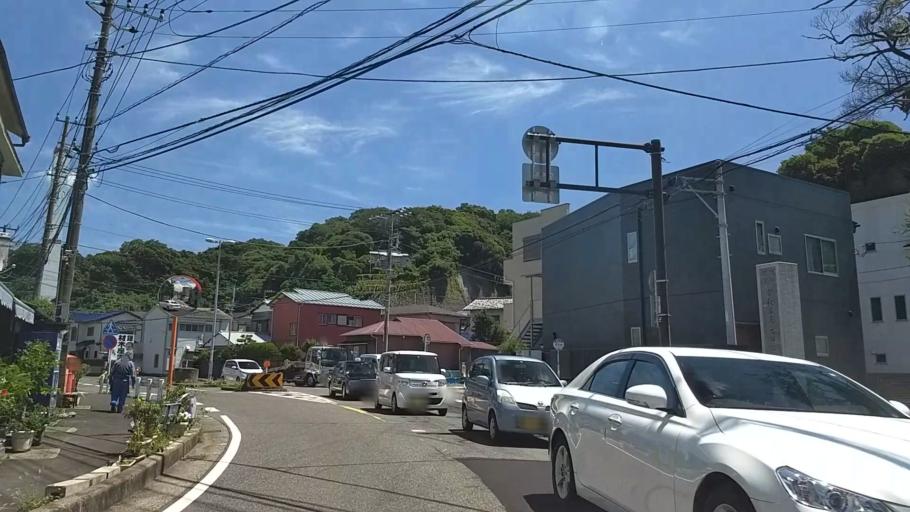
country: JP
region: Kanagawa
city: Kamakura
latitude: 35.3102
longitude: 139.5581
